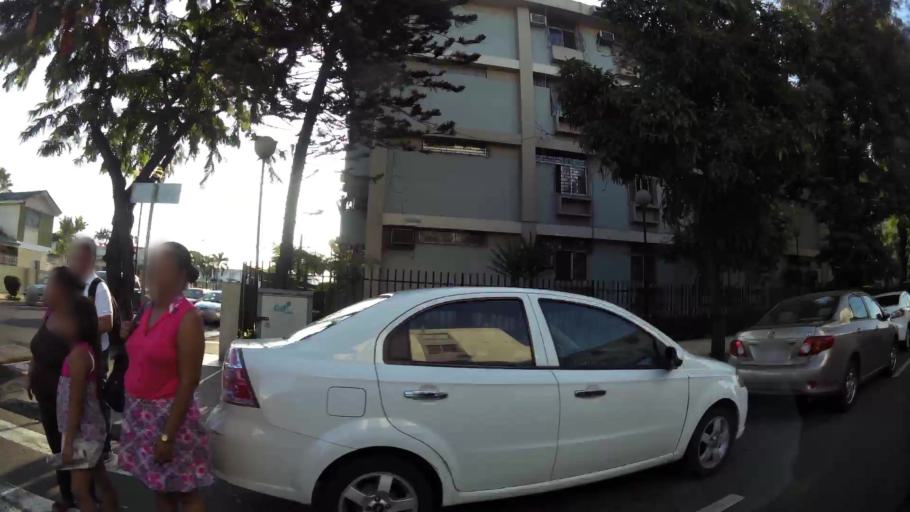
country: EC
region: Guayas
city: Guayaquil
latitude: -2.2160
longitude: -79.8892
